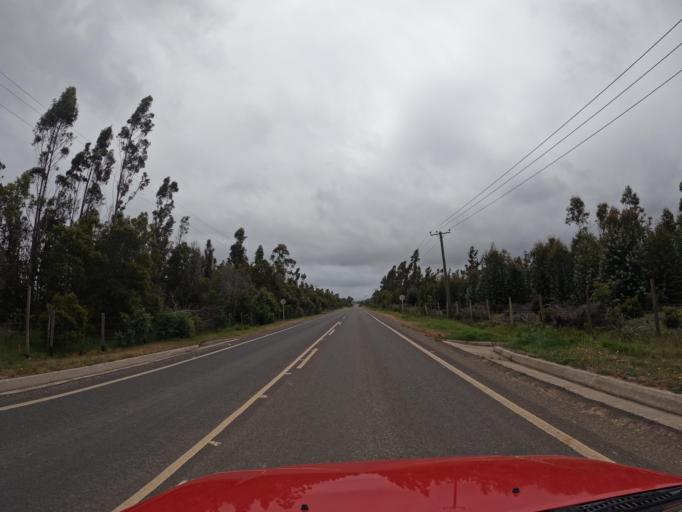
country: CL
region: O'Higgins
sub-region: Provincia de Colchagua
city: Santa Cruz
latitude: -34.5026
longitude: -72.0075
